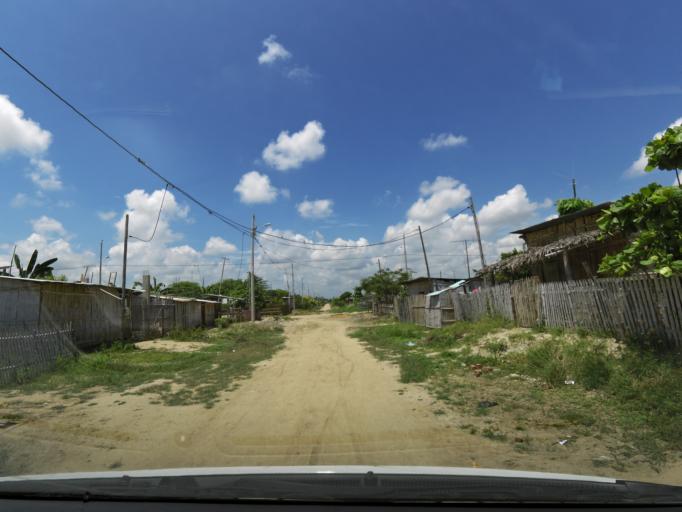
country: EC
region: El Oro
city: Huaquillas
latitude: -3.4729
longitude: -80.2103
